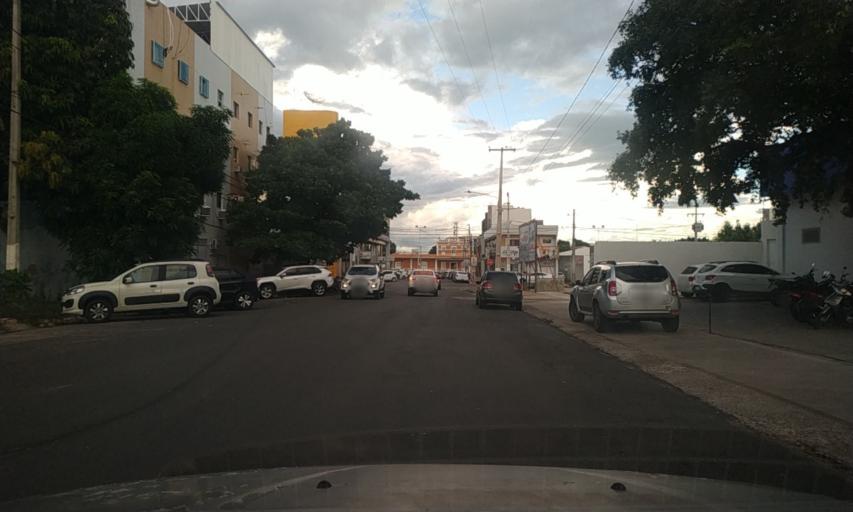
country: BR
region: Rio Grande do Norte
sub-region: Mossoro
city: Mossoro
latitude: -5.1887
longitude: -37.3460
